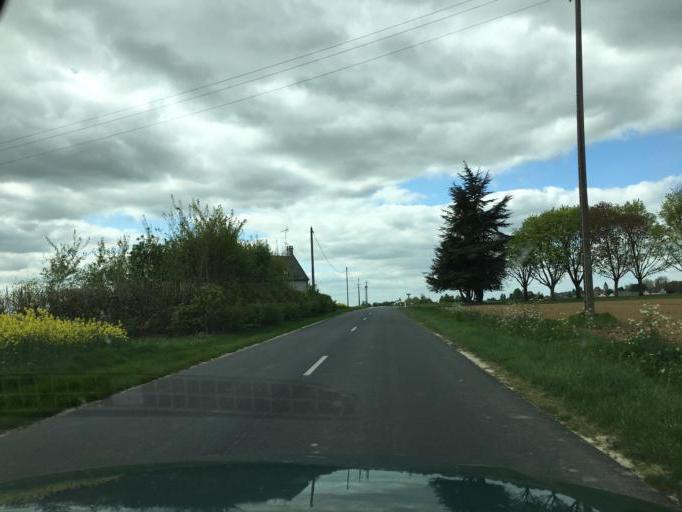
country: FR
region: Centre
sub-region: Departement du Loir-et-Cher
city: Oucques
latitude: 47.8174
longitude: 1.4064
